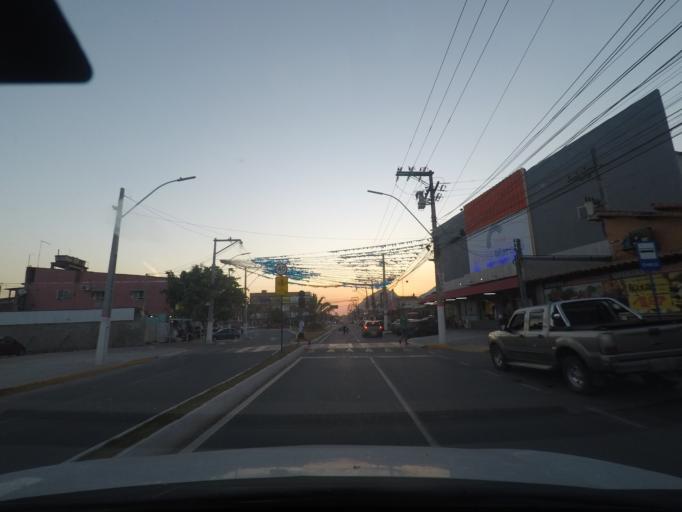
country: BR
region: Rio de Janeiro
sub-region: Niteroi
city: Niteroi
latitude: -22.9569
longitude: -42.9792
